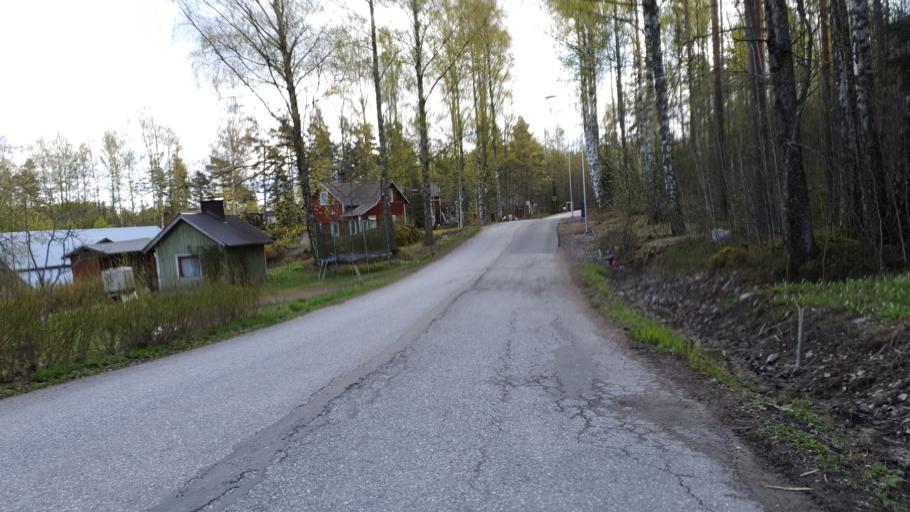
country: FI
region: Uusimaa
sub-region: Helsinki
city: Nurmijaervi
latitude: 60.3495
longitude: 24.8454
